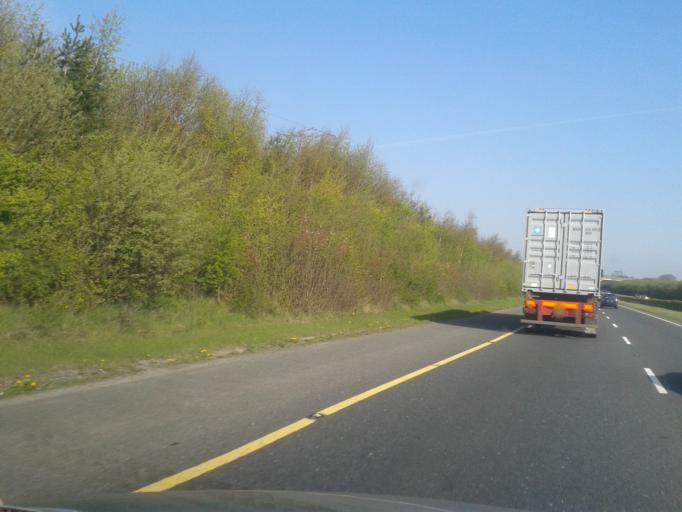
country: IE
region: Leinster
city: Lusk
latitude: 53.5046
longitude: -6.2008
